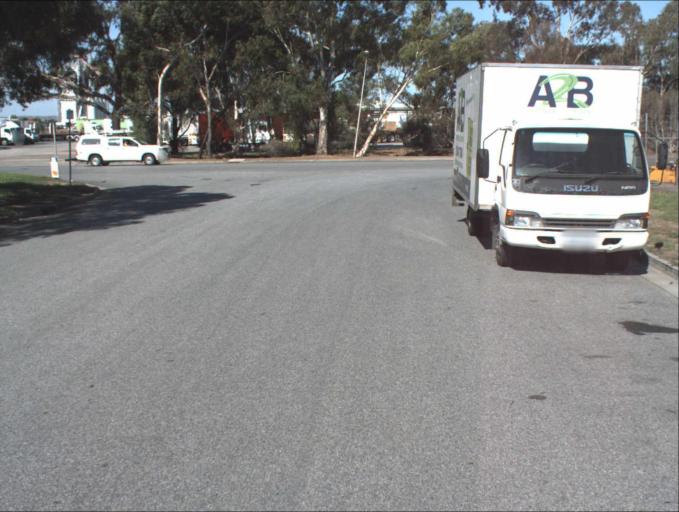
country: AU
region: South Australia
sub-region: Port Adelaide Enfield
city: Blair Athol
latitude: -34.8486
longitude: 138.5685
